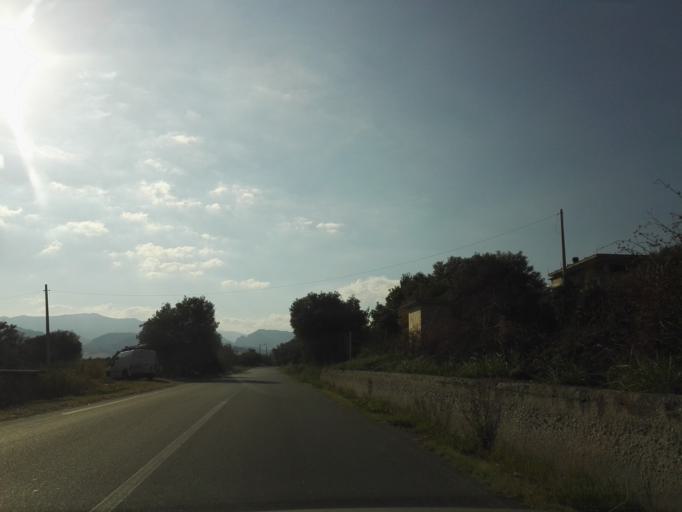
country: IT
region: Calabria
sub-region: Provincia di Reggio Calabria
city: Monasterace
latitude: 38.4399
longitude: 16.5459
